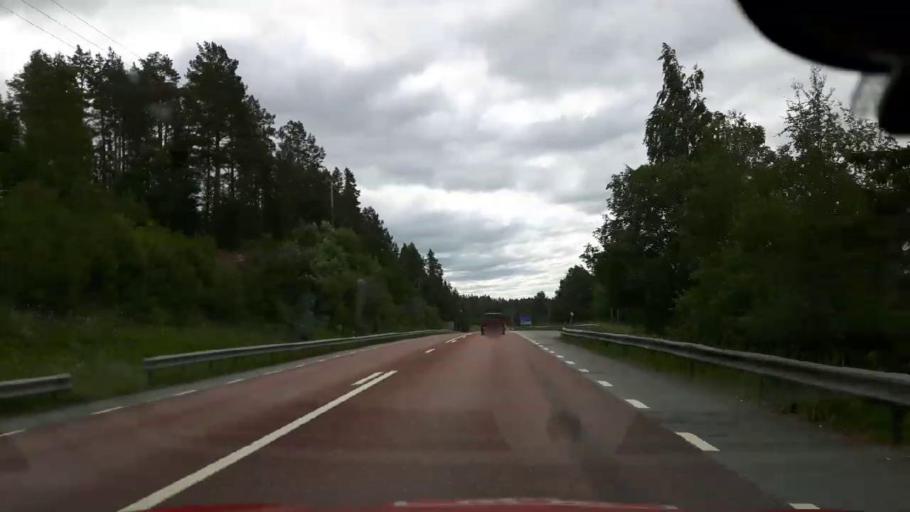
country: SE
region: Jaemtland
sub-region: Braecke Kommun
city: Braecke
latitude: 62.7906
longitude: 15.3780
